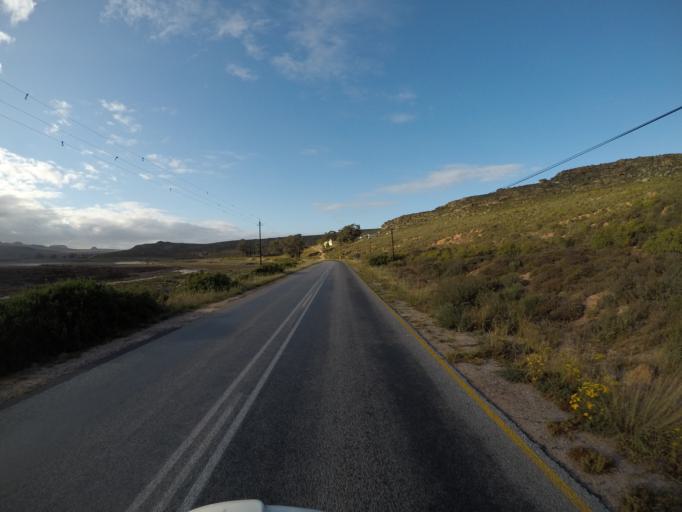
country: ZA
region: Western Cape
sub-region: West Coast District Municipality
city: Clanwilliam
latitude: -32.3193
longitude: 18.3576
